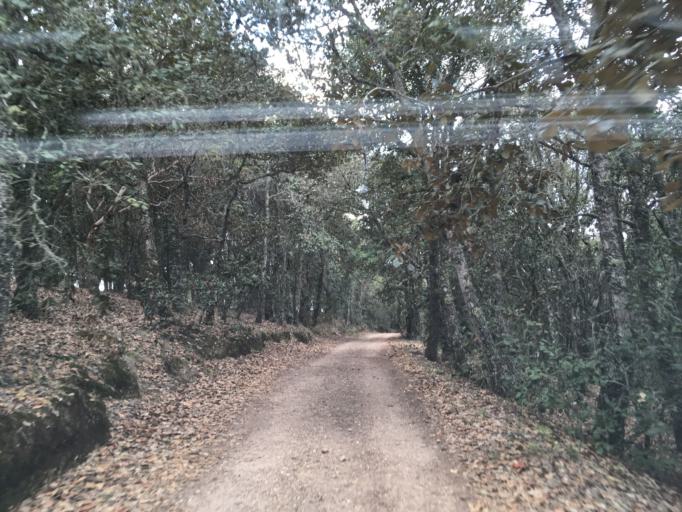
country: MX
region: Oaxaca
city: San Andres Sinaxtla
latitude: 17.6086
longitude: -97.2678
